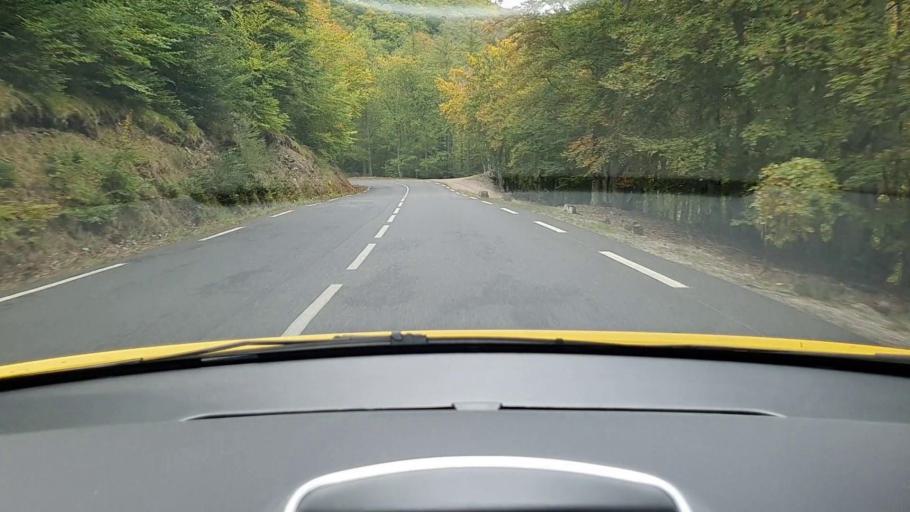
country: FR
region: Languedoc-Roussillon
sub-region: Departement du Gard
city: Valleraugue
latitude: 44.0937
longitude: 3.5618
